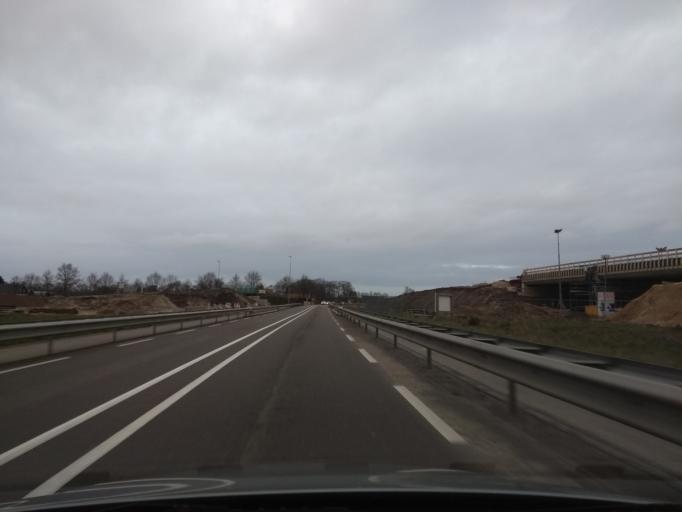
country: NL
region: Overijssel
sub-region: Gemeente Haaksbergen
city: Haaksbergen
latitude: 52.1813
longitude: 6.7379
